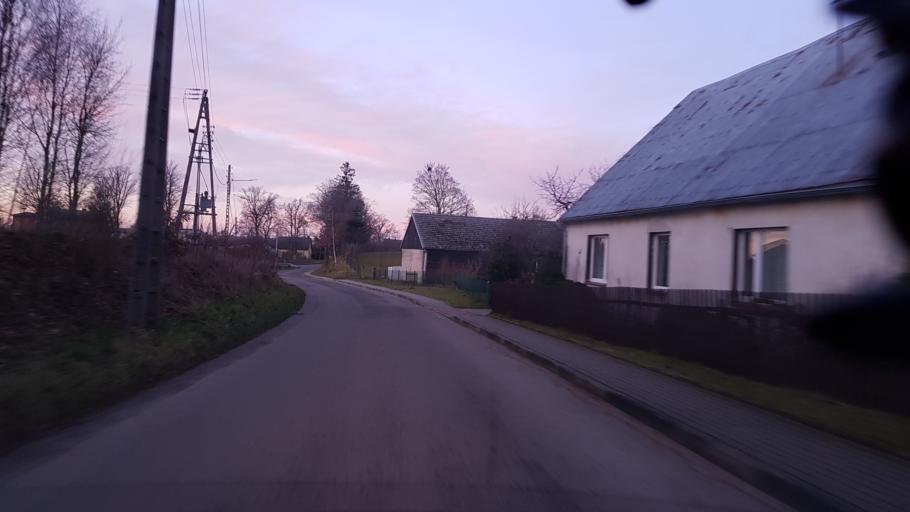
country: PL
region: Pomeranian Voivodeship
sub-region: Powiat bytowski
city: Tuchomie
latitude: 54.1321
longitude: 17.3652
